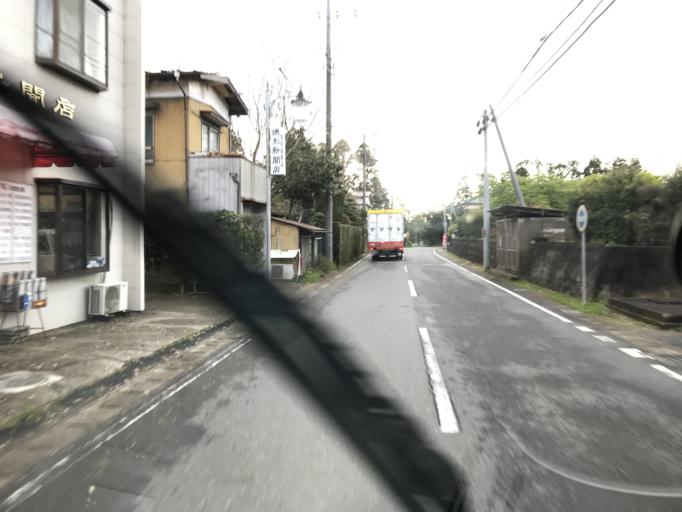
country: JP
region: Chiba
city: Yokaichiba
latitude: 35.7484
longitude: 140.5542
